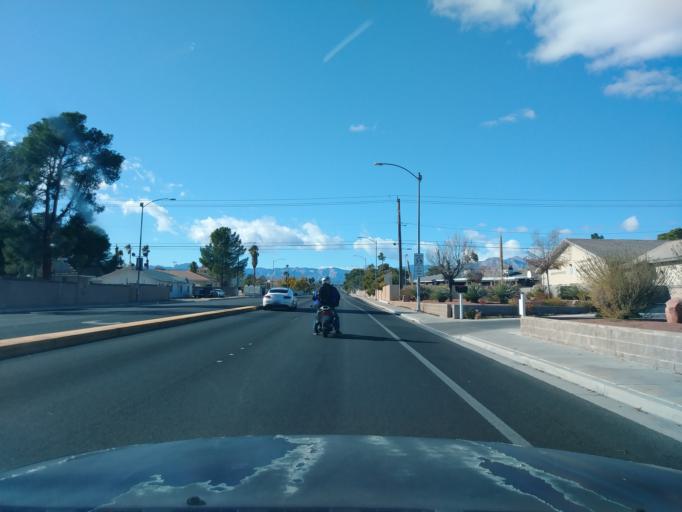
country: US
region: Nevada
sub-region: Clark County
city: Spring Valley
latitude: 36.1519
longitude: -115.2172
